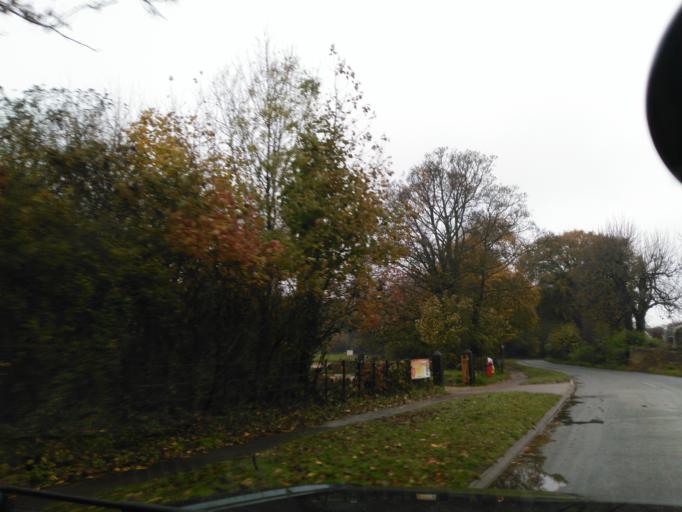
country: GB
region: England
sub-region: Wiltshire
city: Box
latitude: 51.4247
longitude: -2.2253
